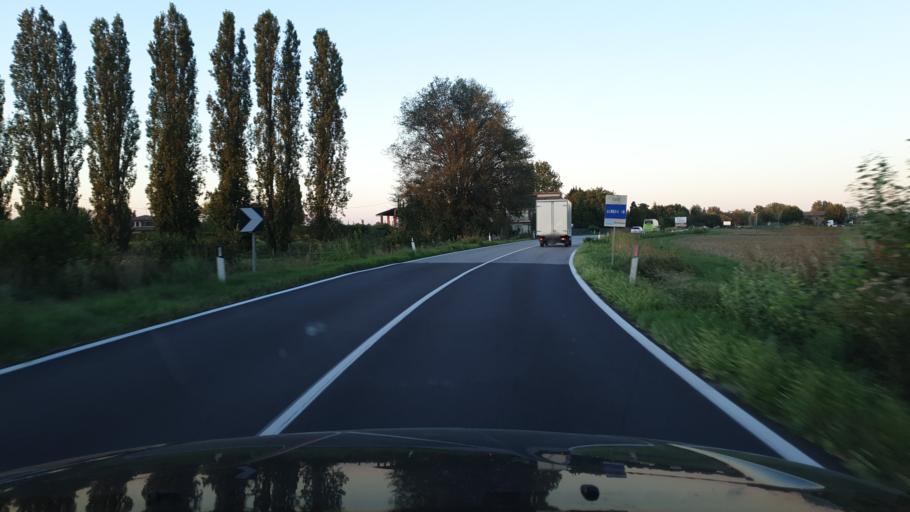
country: IT
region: Emilia-Romagna
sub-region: Provincia di Bologna
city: Progresso
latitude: 44.5726
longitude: 11.4051
